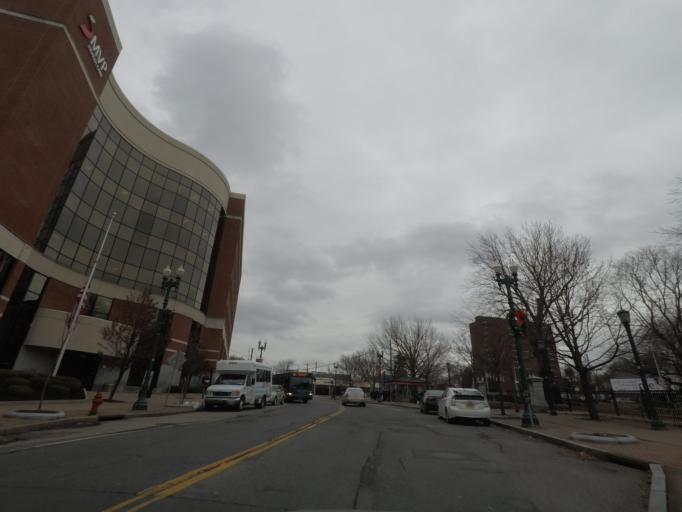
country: US
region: New York
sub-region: Schenectady County
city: Schenectady
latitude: 42.8110
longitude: -73.9387
